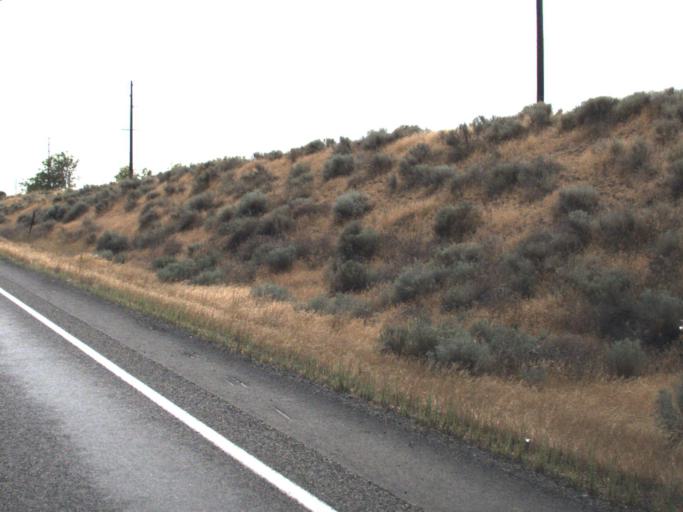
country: US
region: Oregon
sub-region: Morrow County
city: Irrigon
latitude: 45.9585
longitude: -119.6031
